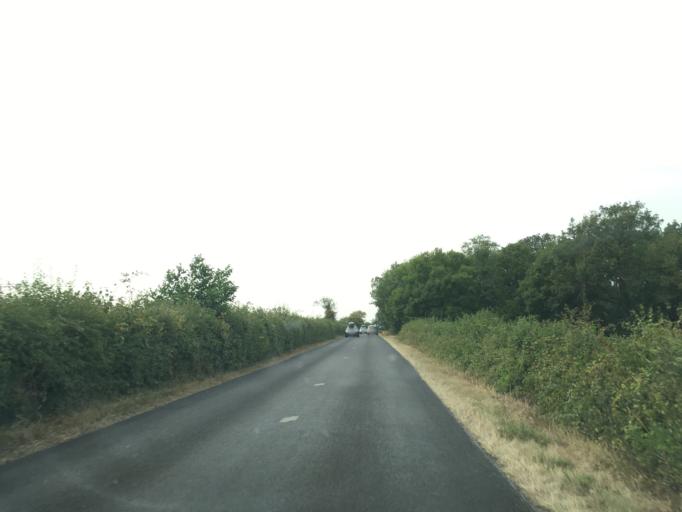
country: FR
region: Midi-Pyrenees
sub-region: Departement du Lot
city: Souillac
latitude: 44.8217
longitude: 1.5796
